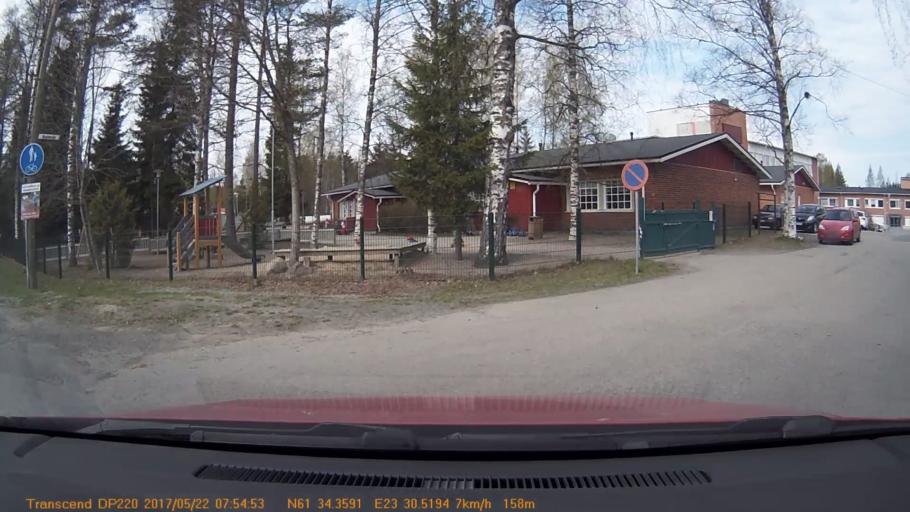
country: FI
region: Pirkanmaa
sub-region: Tampere
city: Yloejaervi
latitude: 61.5727
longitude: 23.5087
